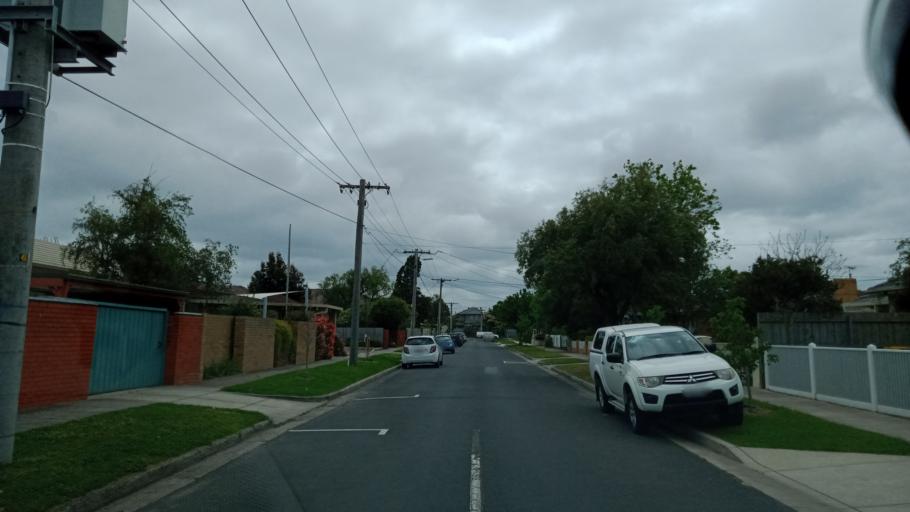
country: AU
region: Victoria
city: McKinnon
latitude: -37.9220
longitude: 145.0675
